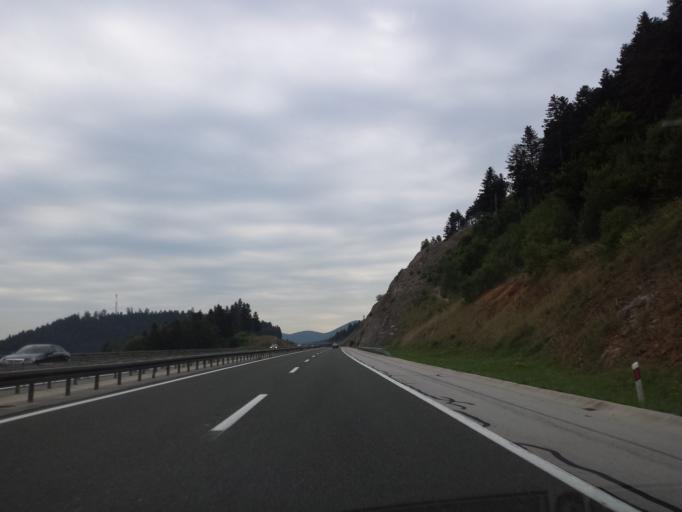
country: HR
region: Licko-Senjska
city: Otocac
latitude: 44.8538
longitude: 15.2253
